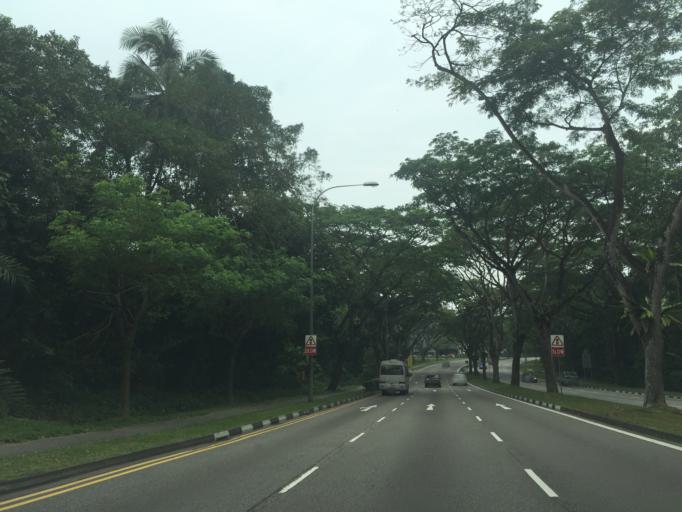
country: SG
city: Singapore
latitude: 1.3850
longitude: 103.8236
